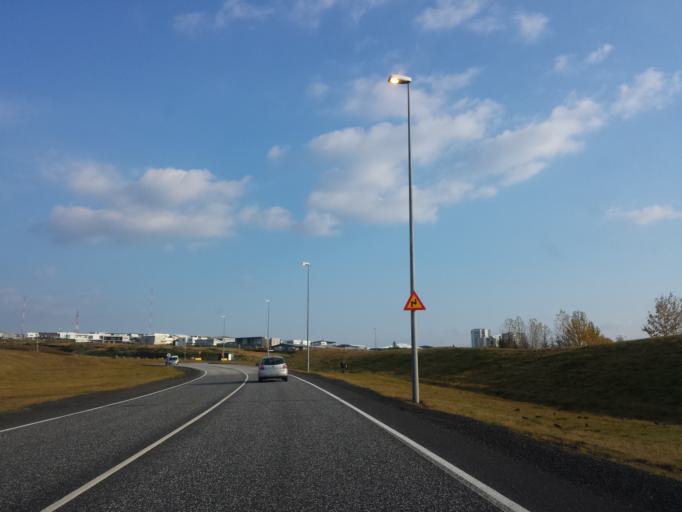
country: IS
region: Capital Region
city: Reykjavik
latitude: 64.0890
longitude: -21.8396
